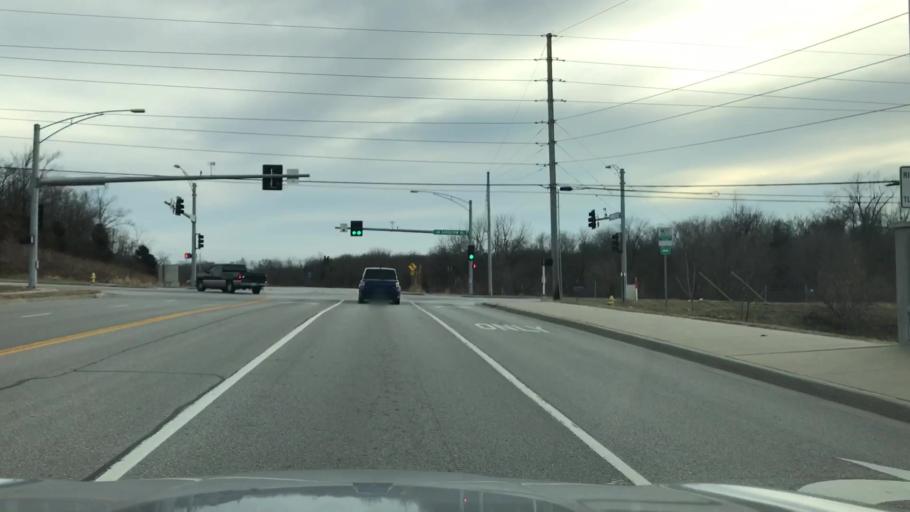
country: US
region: Missouri
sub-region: Jackson County
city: Lees Summit
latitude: 38.9051
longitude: -94.4148
